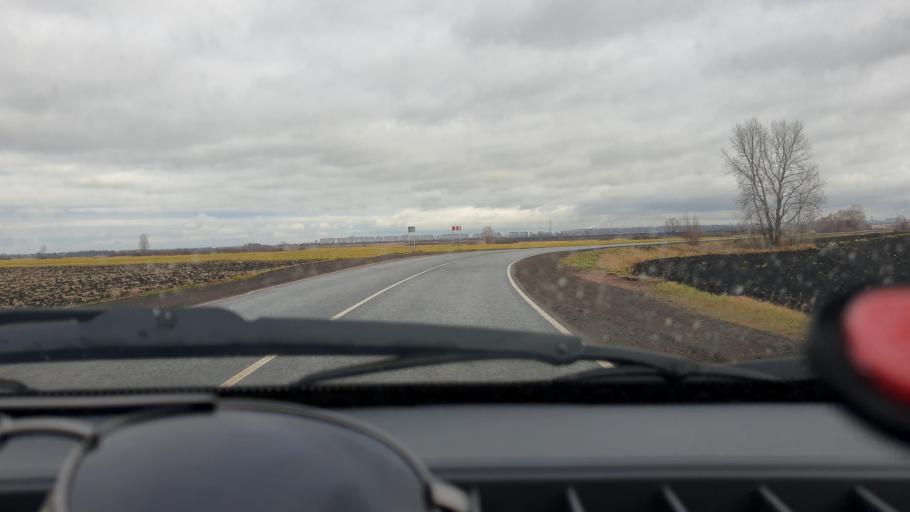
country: RU
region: Bashkortostan
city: Ufa
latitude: 54.8081
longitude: 55.9657
